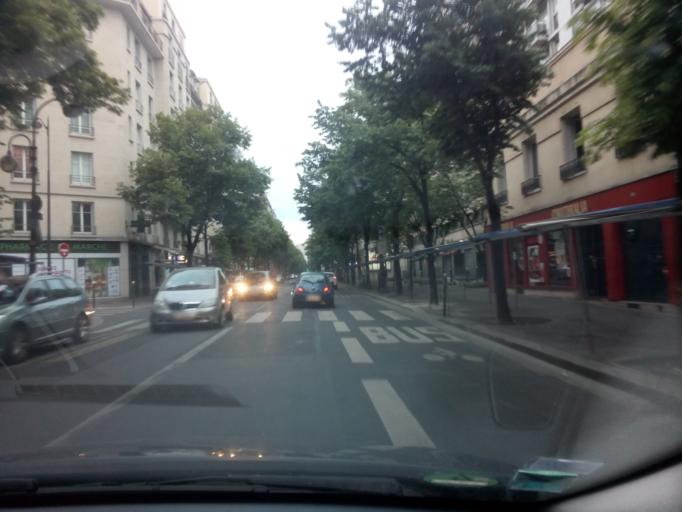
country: FR
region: Ile-de-France
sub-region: Departement des Hauts-de-Seine
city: Vanves
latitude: 48.8366
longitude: 2.2987
